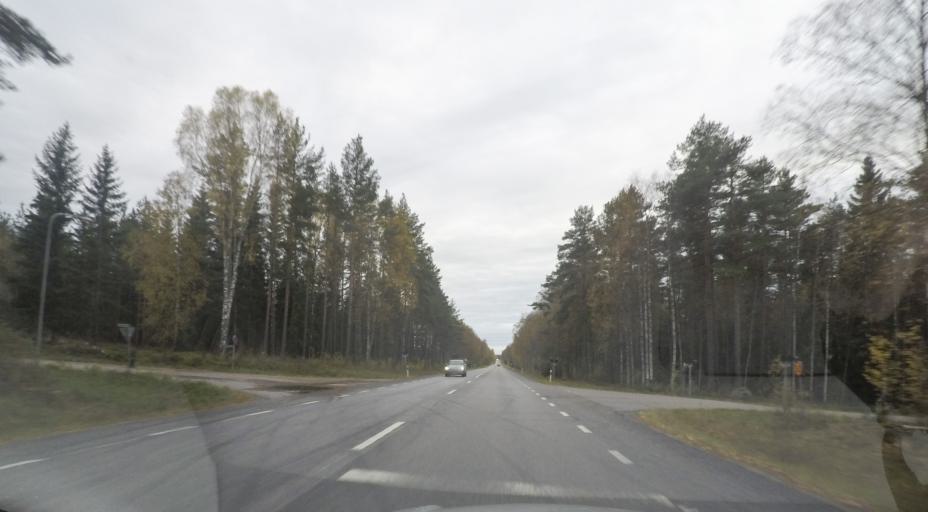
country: SE
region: OErebro
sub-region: Hallefors Kommun
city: Haellefors
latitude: 59.7656
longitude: 14.5205
